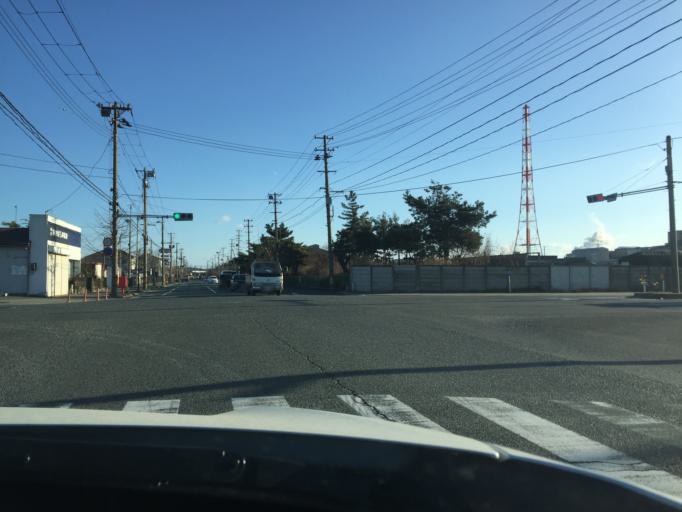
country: JP
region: Fukushima
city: Iwaki
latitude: 36.9428
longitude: 140.8745
